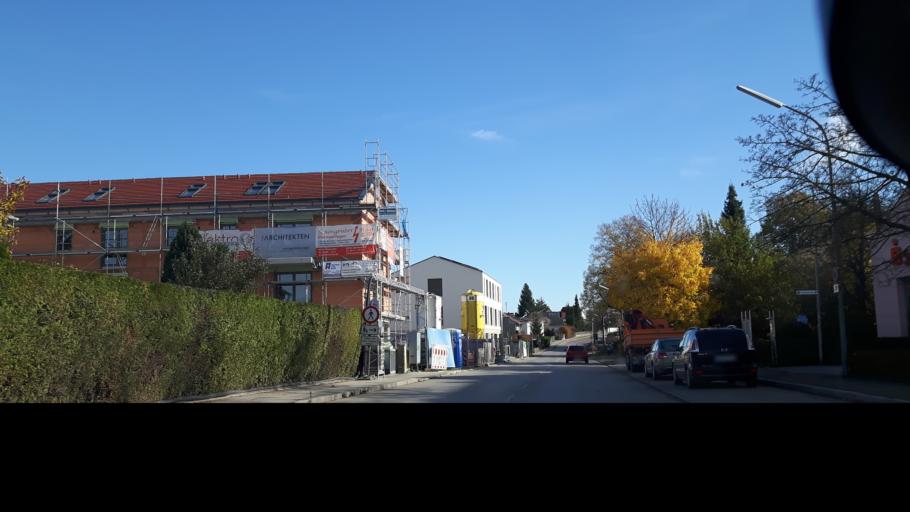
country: DE
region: Bavaria
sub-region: Upper Bavaria
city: Schwabhausen
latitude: 48.3030
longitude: 11.3570
